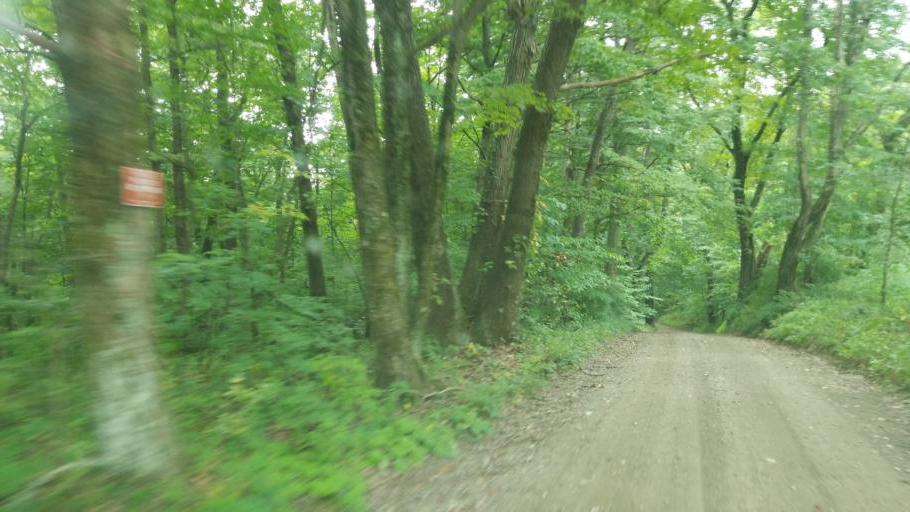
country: US
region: Ohio
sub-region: Ashland County
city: Loudonville
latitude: 40.5909
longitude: -82.2951
